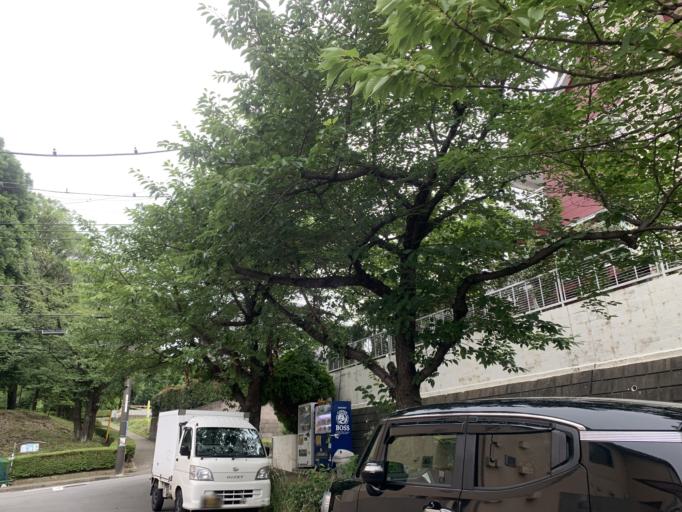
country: JP
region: Tokyo
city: Chofugaoka
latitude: 35.5567
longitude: 139.5976
